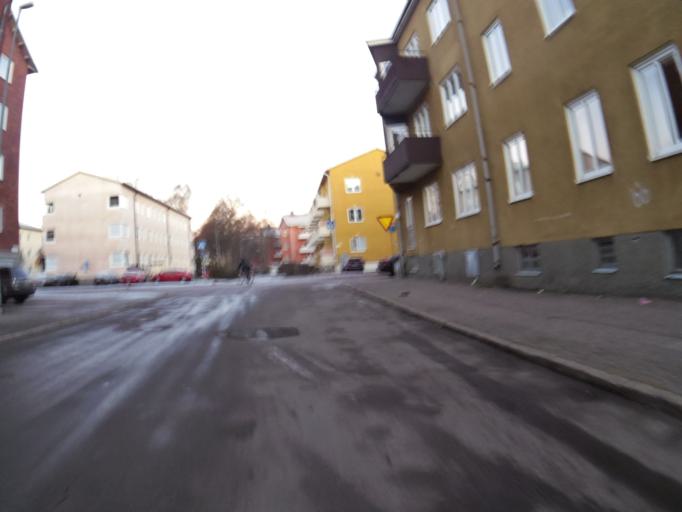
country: SE
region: Gaevleborg
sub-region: Gavle Kommun
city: Gavle
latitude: 60.6690
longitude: 17.1448
